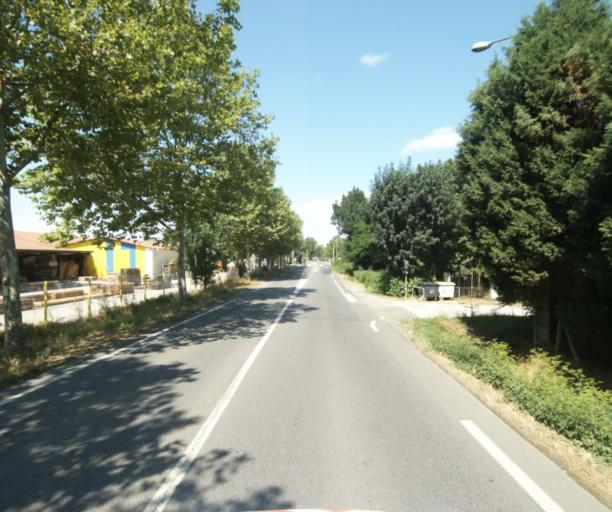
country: FR
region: Midi-Pyrenees
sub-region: Departement de la Haute-Garonne
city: Revel
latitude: 43.4686
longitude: 2.0110
